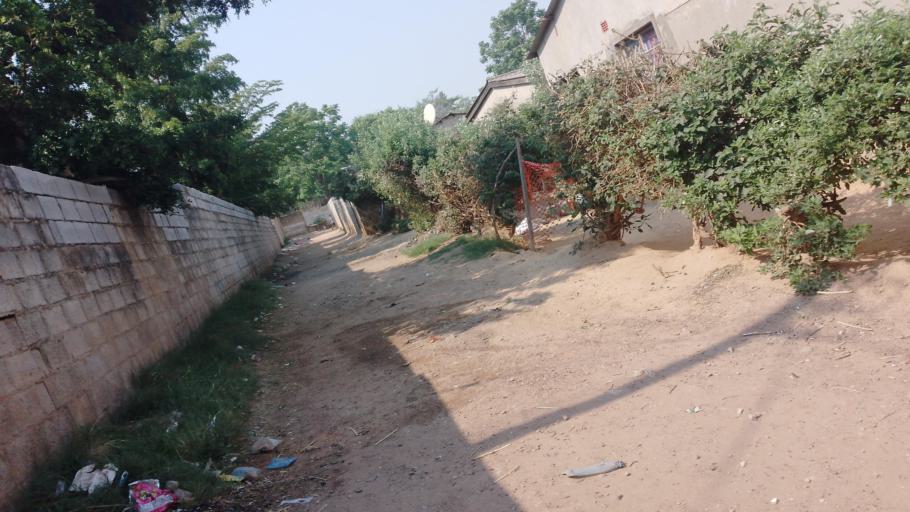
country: ZM
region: Lusaka
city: Lusaka
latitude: -15.4014
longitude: 28.3658
